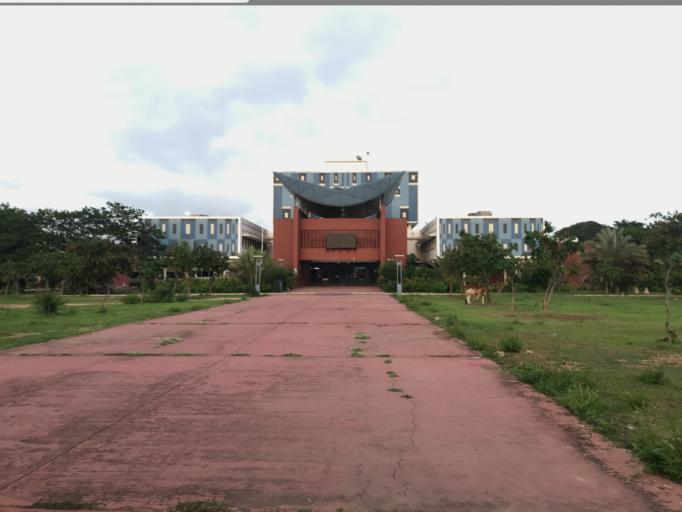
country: SN
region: Dakar
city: Dakar
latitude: 14.6855
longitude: -17.4633
